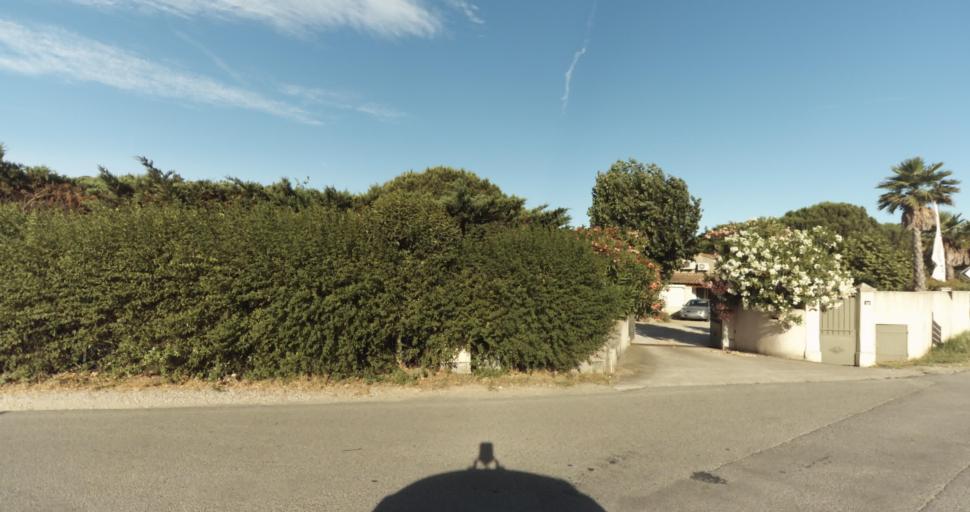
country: FR
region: Provence-Alpes-Cote d'Azur
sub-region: Departement du Var
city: Saint-Tropez
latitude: 43.2549
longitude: 6.6374
